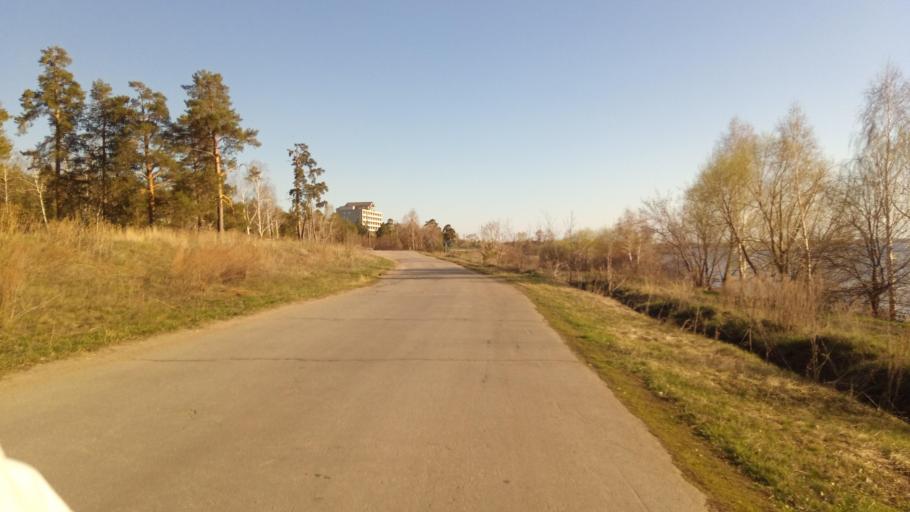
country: RU
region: Chelyabinsk
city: Novosineglazovskiy
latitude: 55.1283
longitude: 61.3282
